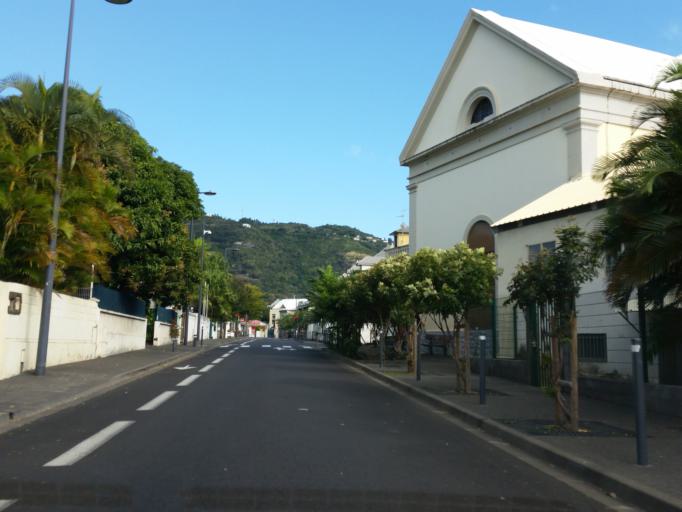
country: RE
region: Reunion
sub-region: Reunion
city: Saint-Denis
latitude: -20.8856
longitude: 55.4529
